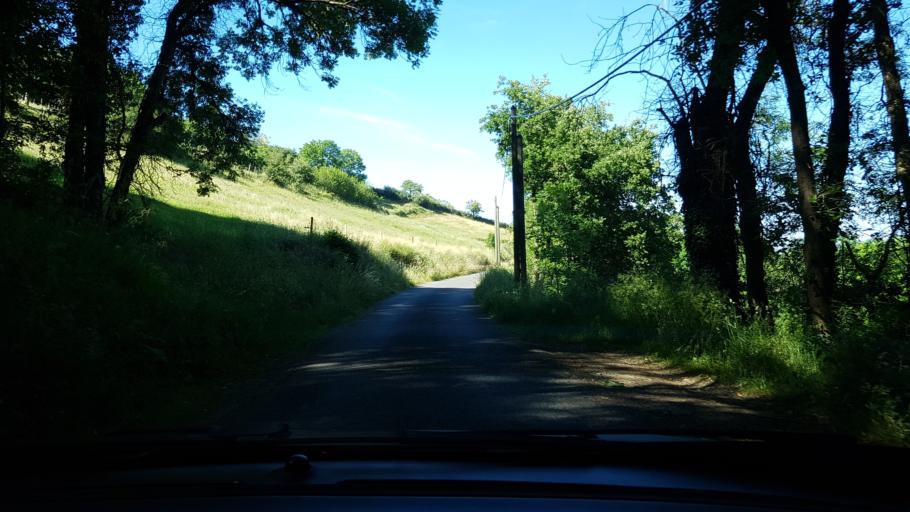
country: FR
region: Rhone-Alpes
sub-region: Departement du Rhone
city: Saint-Didier-sous-Riverie
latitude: 45.5835
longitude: 4.5884
